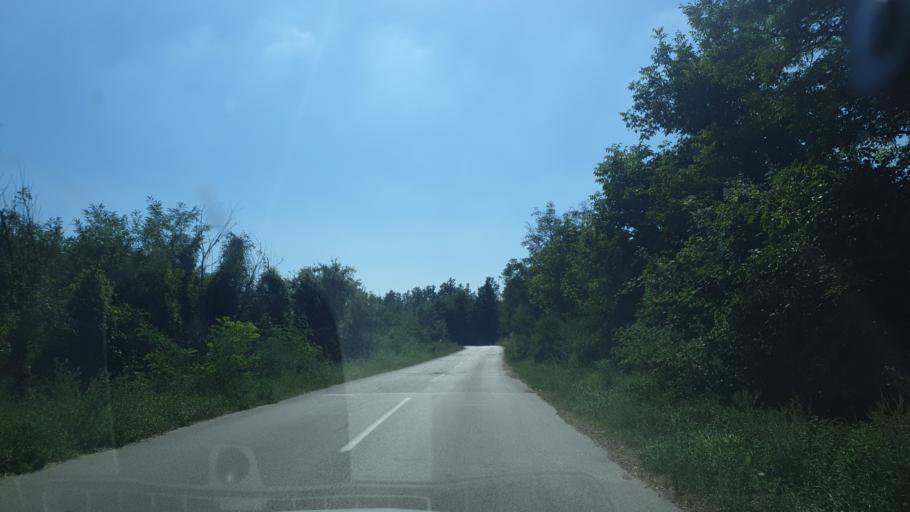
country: RS
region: Central Serbia
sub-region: Zlatiborski Okrug
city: Kosjeric
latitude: 43.9907
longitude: 20.0485
